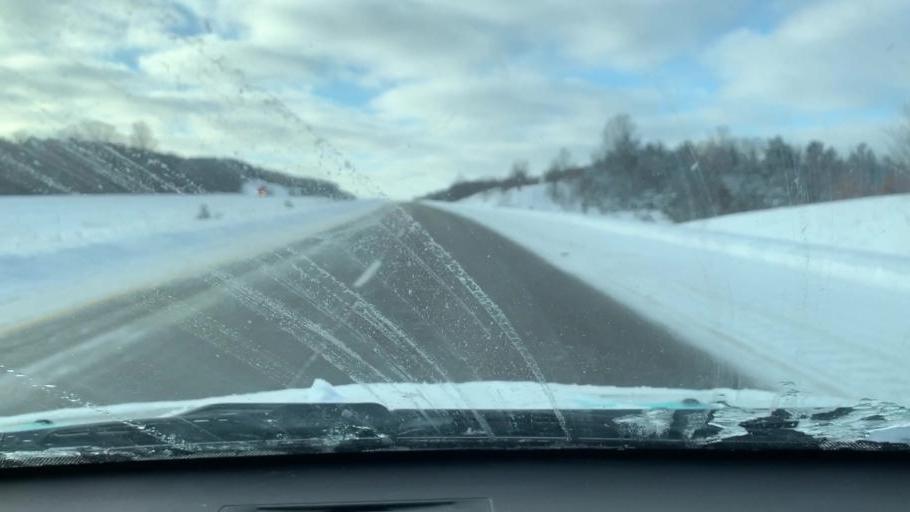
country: US
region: Michigan
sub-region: Wexford County
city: Manton
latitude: 44.3661
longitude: -85.4024
